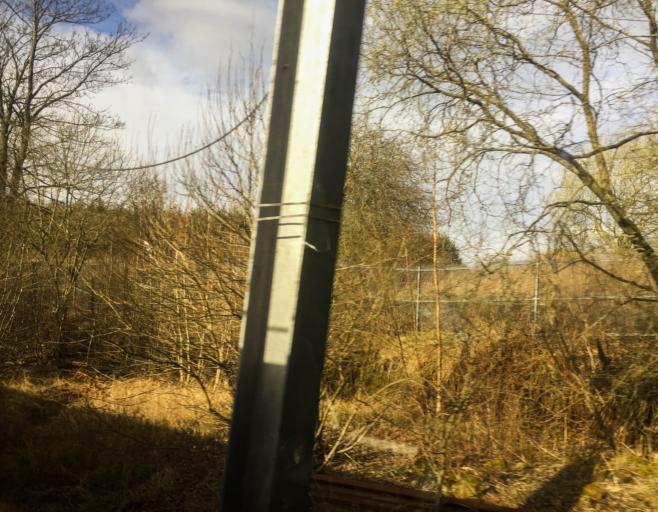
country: GB
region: Scotland
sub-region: North Lanarkshire
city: Glenboig
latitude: 55.8786
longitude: -4.0480
